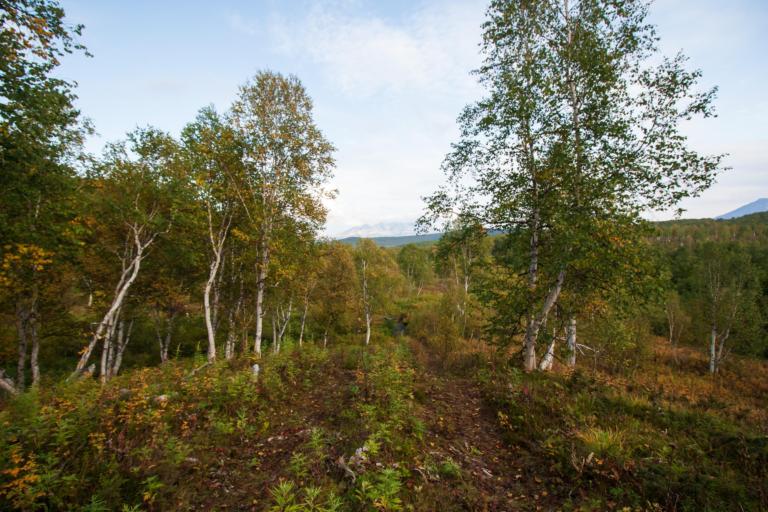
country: RU
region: Kamtsjatka
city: Yelizovo
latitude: 53.7512
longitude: 158.6329
